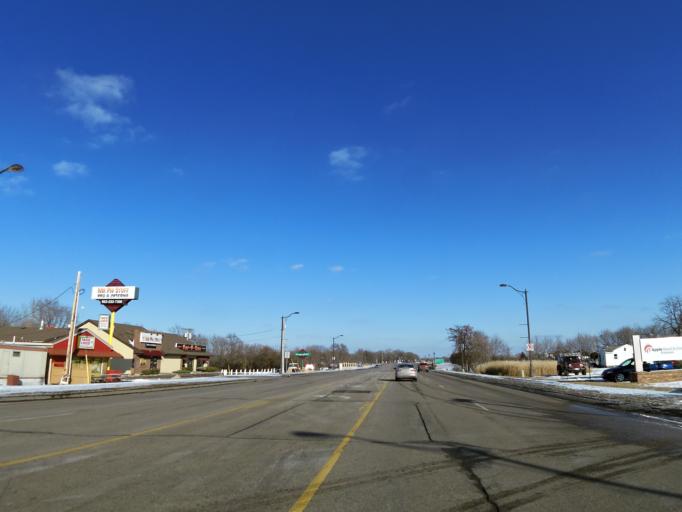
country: US
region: Minnesota
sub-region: Scott County
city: Shakopee
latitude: 44.8010
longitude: -93.5070
